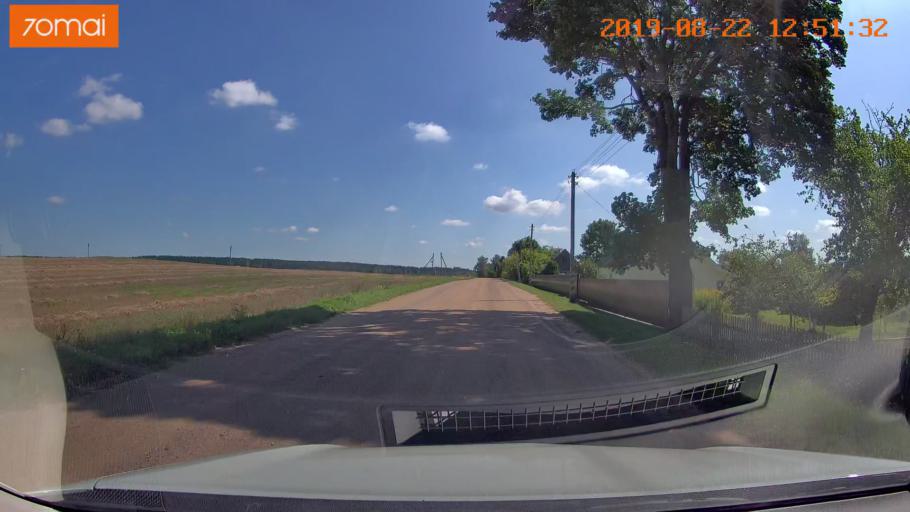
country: BY
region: Minsk
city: Prawdzinski
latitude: 53.4575
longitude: 27.6564
